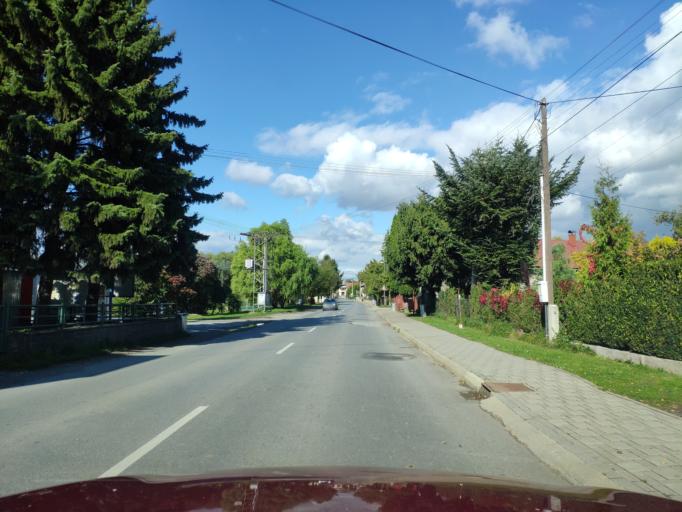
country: SK
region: Presovsky
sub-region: Okres Presov
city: Presov
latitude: 48.9531
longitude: 21.3051
